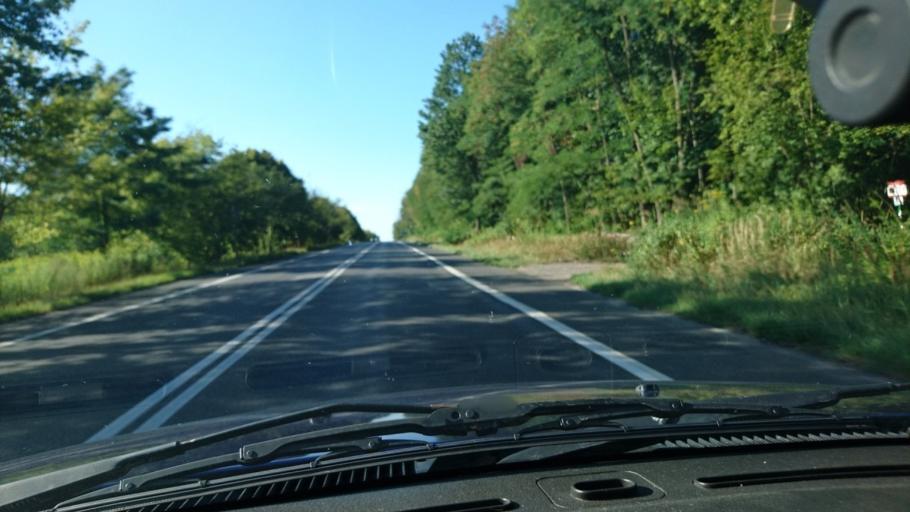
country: PL
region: Silesian Voivodeship
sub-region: Powiat gliwicki
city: Pyskowice
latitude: 50.3552
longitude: 18.6444
